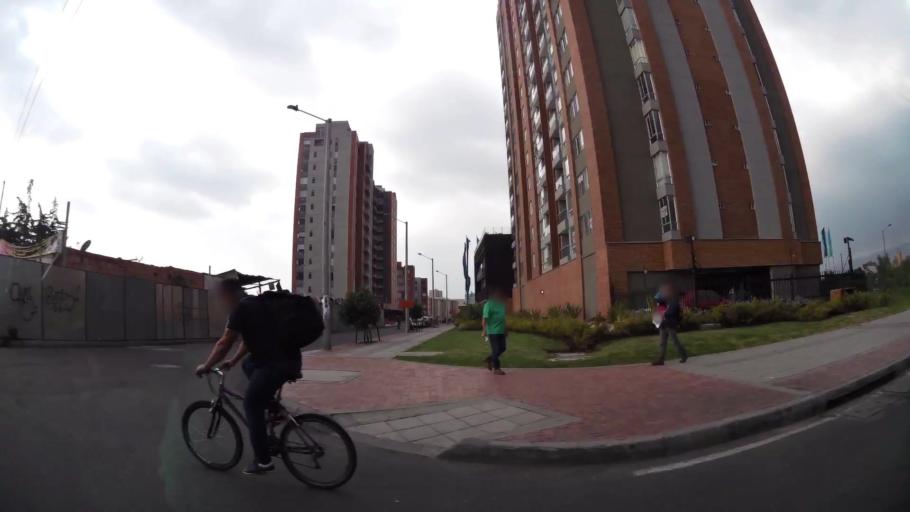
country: CO
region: Bogota D.C.
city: Barrio San Luis
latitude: 4.7165
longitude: -74.0614
